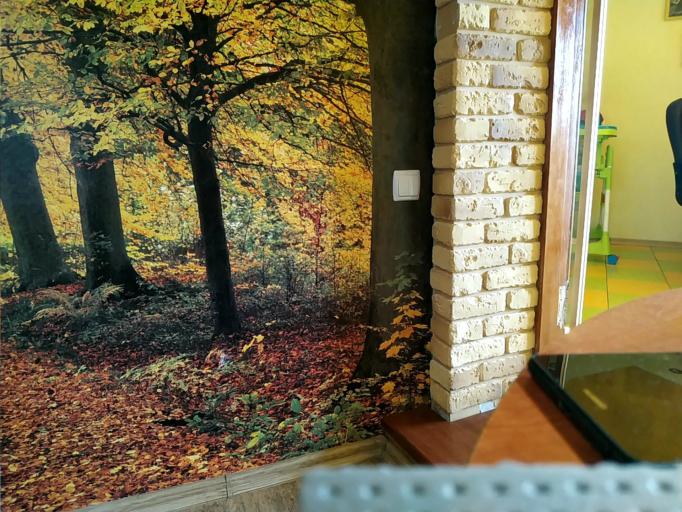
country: RU
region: Tverskaya
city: Zubtsov
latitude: 56.2088
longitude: 34.5416
